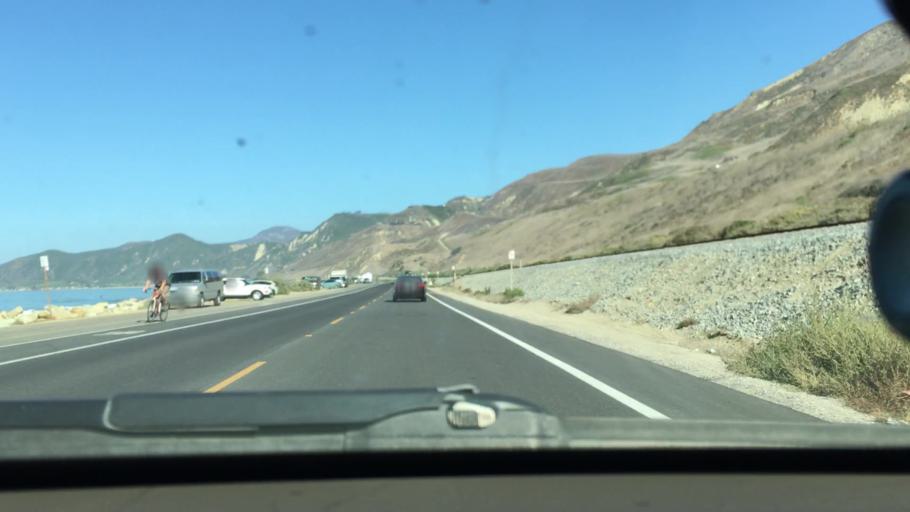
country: US
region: California
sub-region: Ventura County
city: Ventura
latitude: 34.2988
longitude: -119.3437
